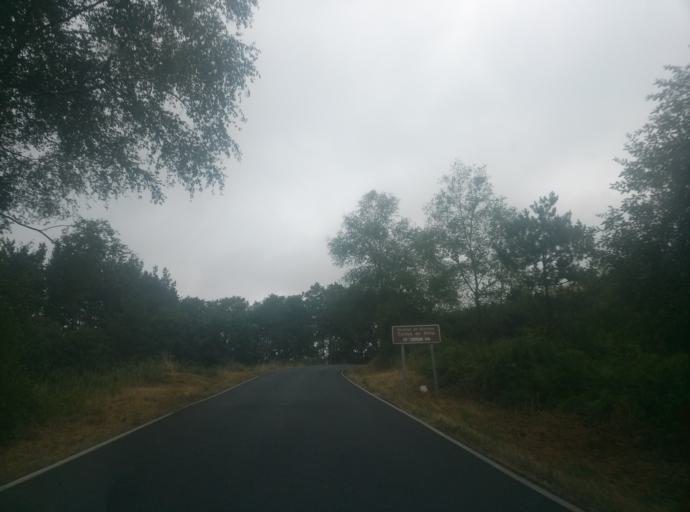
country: ES
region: Galicia
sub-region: Provincia de Lugo
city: Lugo
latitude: 43.0762
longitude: -7.5496
